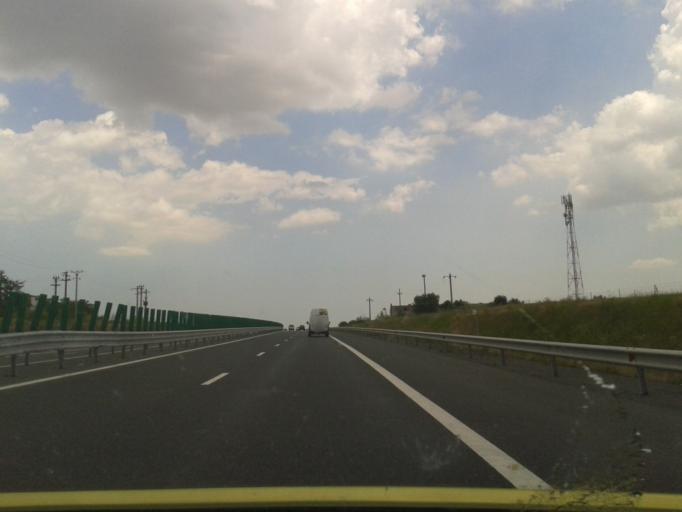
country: RO
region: Constanta
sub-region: Comuna Mircea Voda
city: Satu Nou
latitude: 44.2181
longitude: 28.1987
